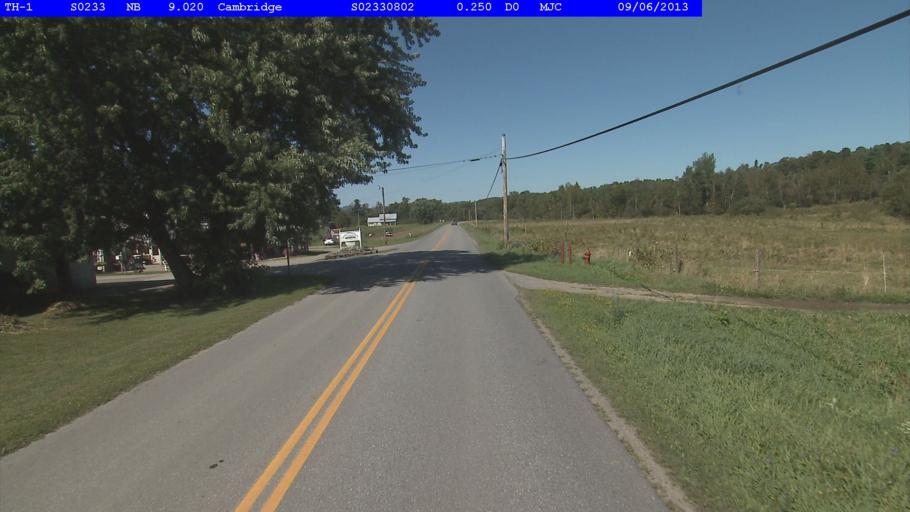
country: US
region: Vermont
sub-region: Chittenden County
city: Jericho
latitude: 44.5884
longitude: -72.8635
